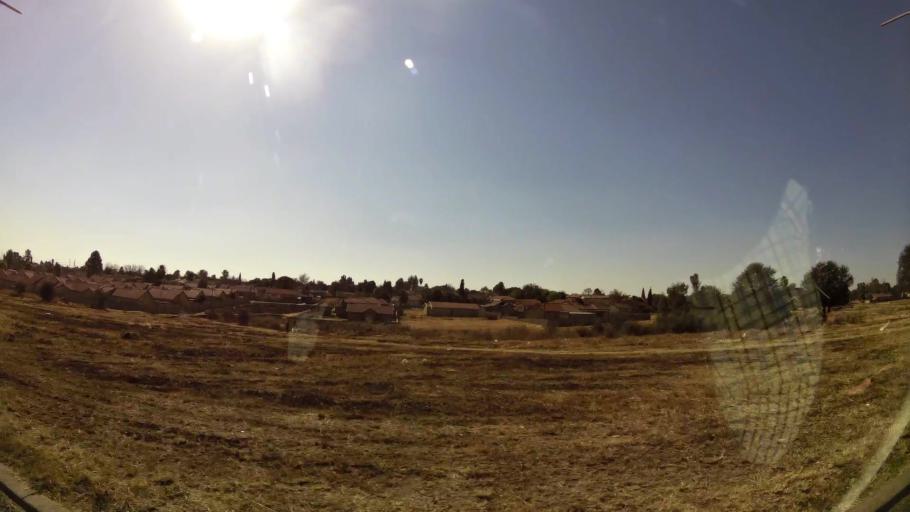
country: ZA
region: Gauteng
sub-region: Ekurhuleni Metropolitan Municipality
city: Tembisa
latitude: -26.0402
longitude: 28.2308
